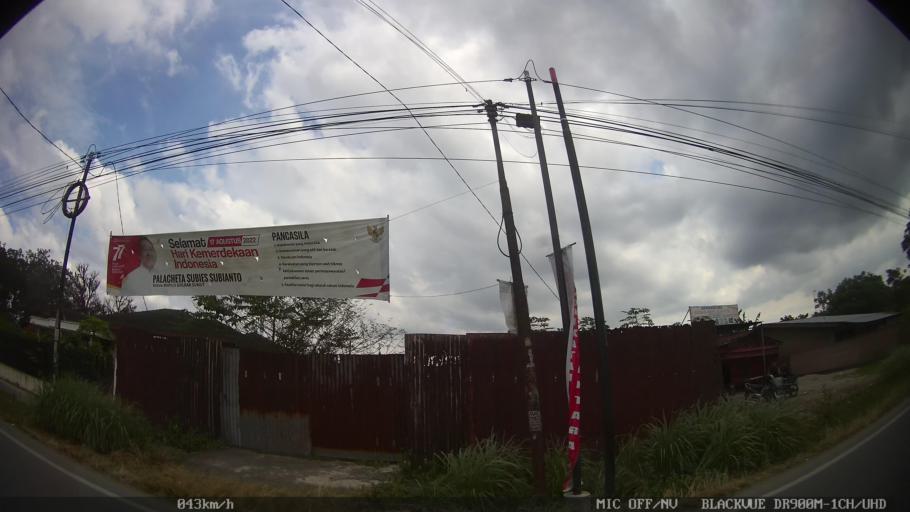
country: ID
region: North Sumatra
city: Sunggal
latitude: 3.6181
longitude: 98.6207
